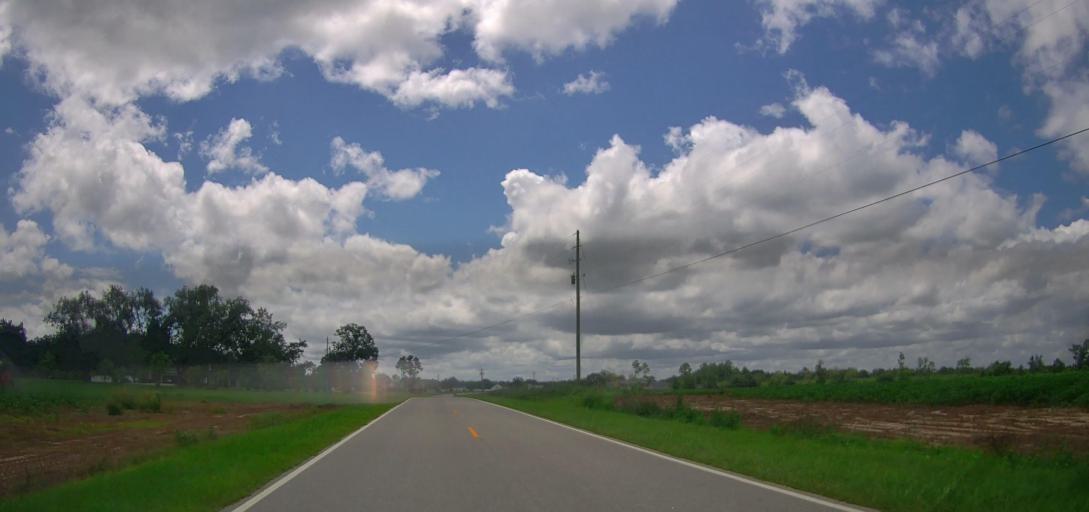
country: US
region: Georgia
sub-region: Irwin County
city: Ocilla
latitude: 31.6435
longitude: -83.2658
